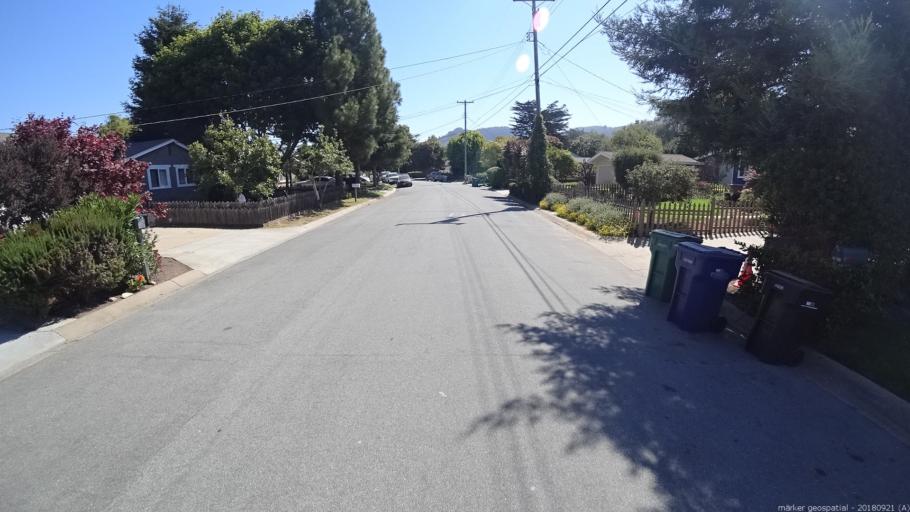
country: US
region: California
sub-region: Monterey County
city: Carmel-by-the-Sea
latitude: 36.5394
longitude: -121.9156
